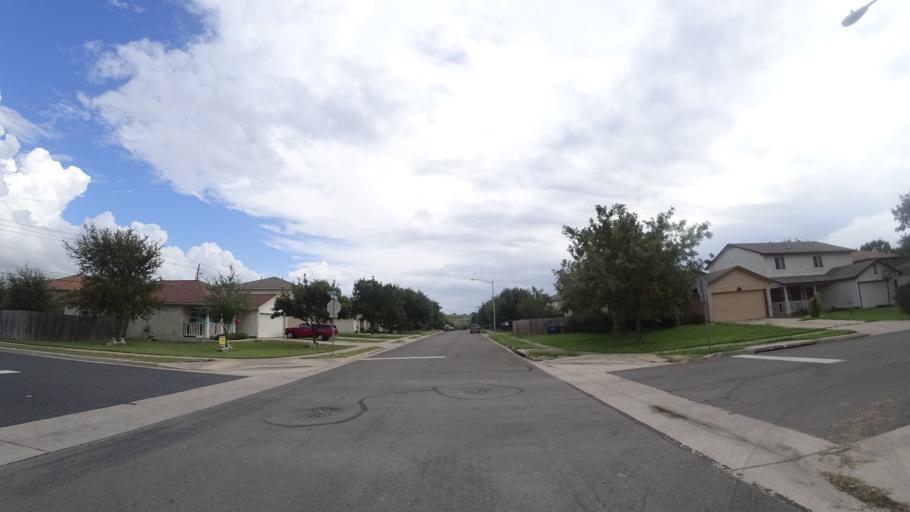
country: US
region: Texas
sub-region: Travis County
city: Onion Creek
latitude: 30.1554
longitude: -97.7388
